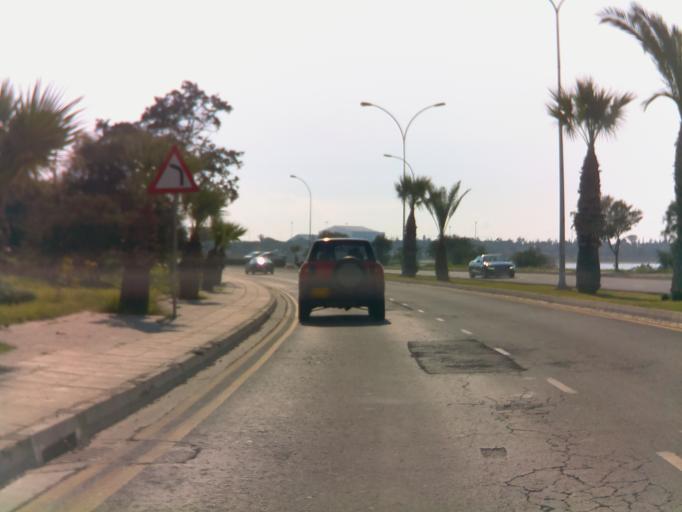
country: CY
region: Larnaka
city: Larnaca
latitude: 34.8972
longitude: 33.6305
